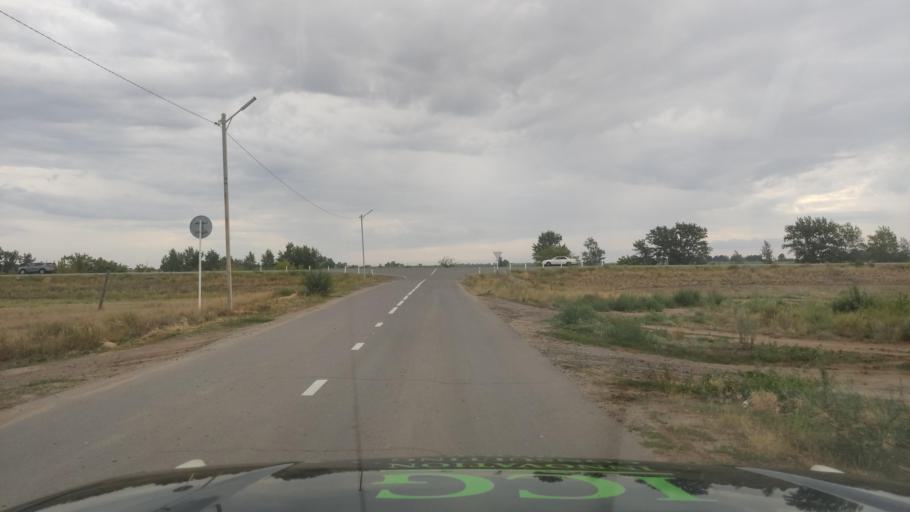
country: KZ
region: Pavlodar
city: Leninskiy
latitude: 52.5404
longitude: 76.8115
